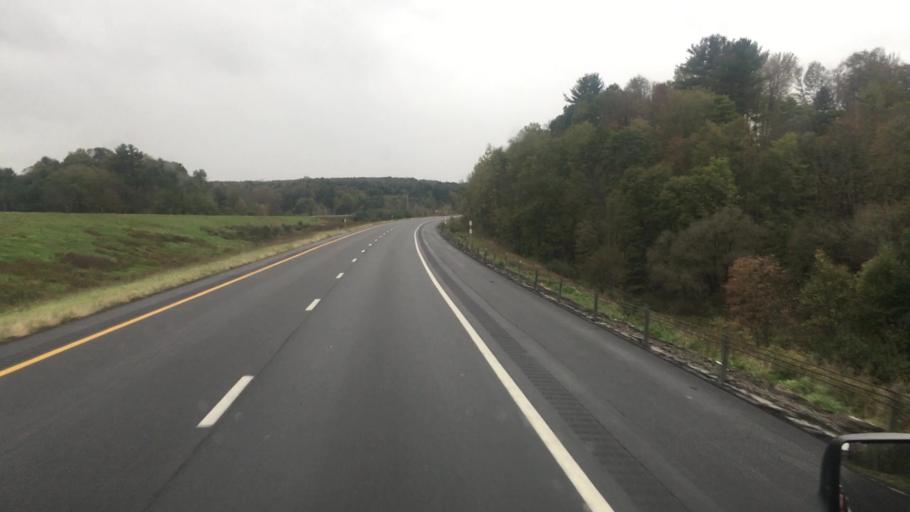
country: US
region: New York
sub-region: Chenango County
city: Bainbridge
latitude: 42.1991
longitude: -75.5359
